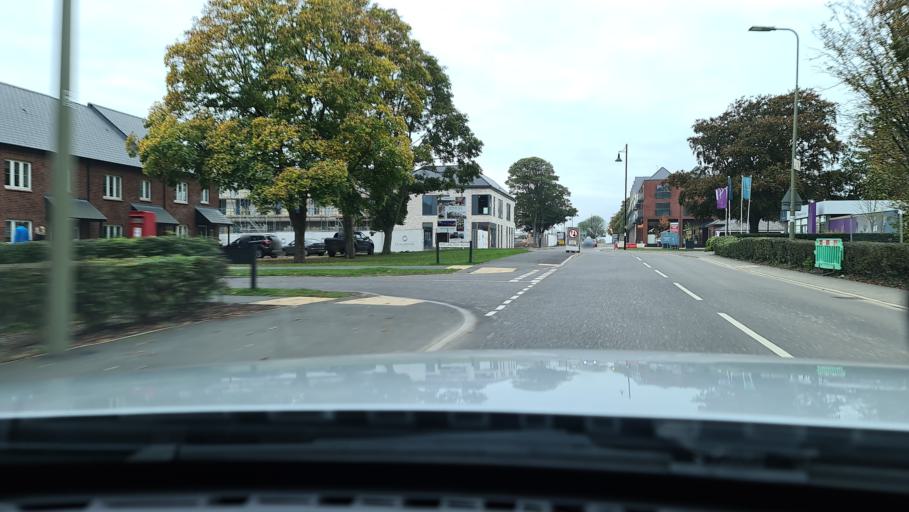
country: GB
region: England
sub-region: Oxfordshire
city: Somerton
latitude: 51.9280
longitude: -1.2521
